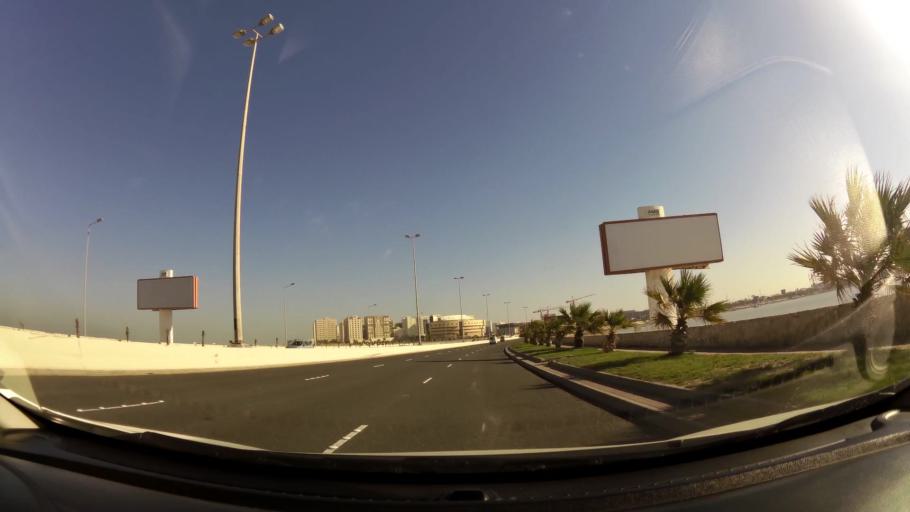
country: BH
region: Muharraq
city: Al Muharraq
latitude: 26.2565
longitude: 50.5945
